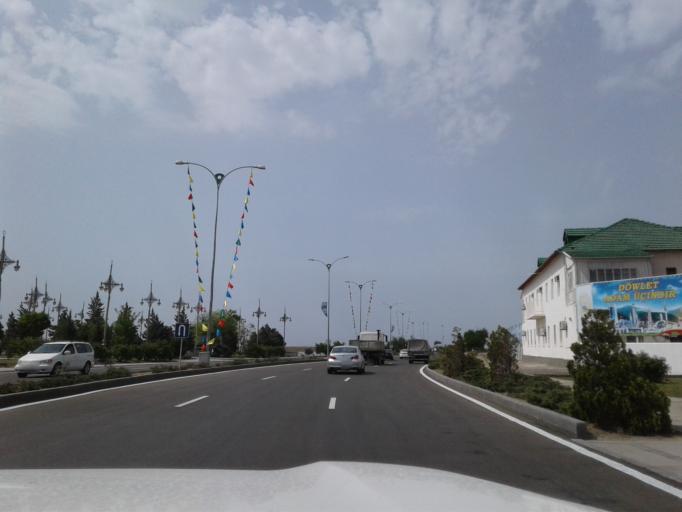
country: TM
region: Balkan
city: Turkmenbasy
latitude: 39.9924
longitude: 52.9880
